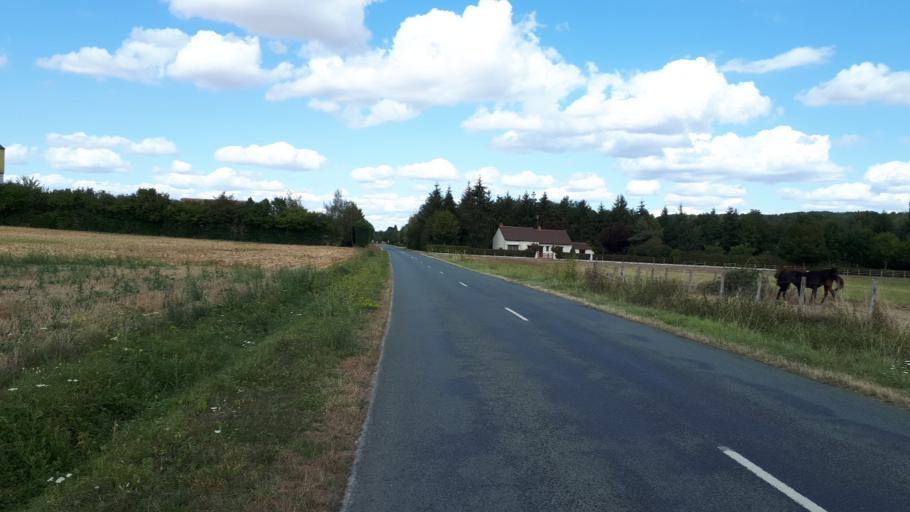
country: FR
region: Centre
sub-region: Departement du Loir-et-Cher
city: Aze
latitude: 47.8443
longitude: 0.9914
